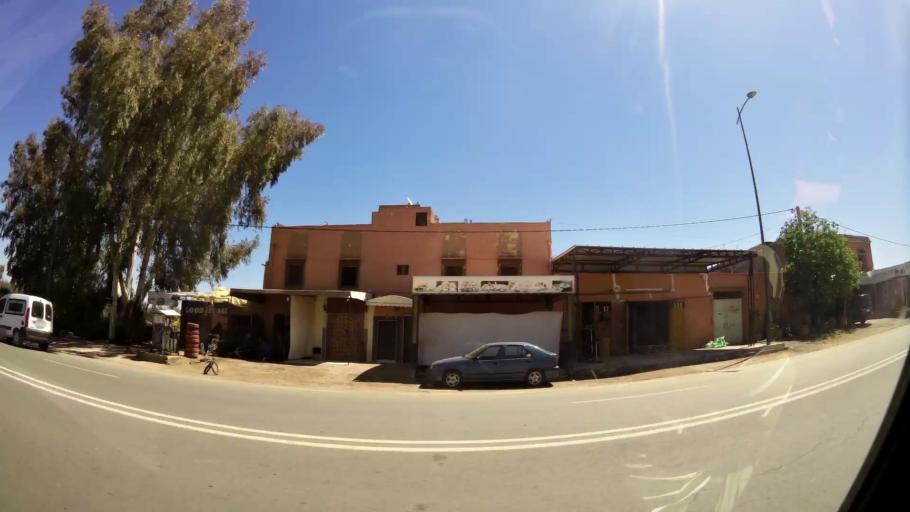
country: MA
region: Marrakech-Tensift-Al Haouz
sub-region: Marrakech
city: Marrakesh
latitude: 31.5633
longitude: -7.9792
